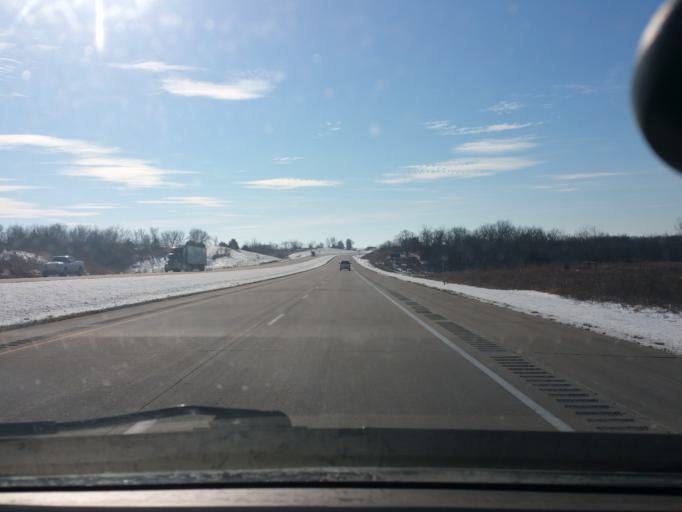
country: US
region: Iowa
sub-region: Clarke County
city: Osceola
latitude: 40.9082
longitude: -93.7971
